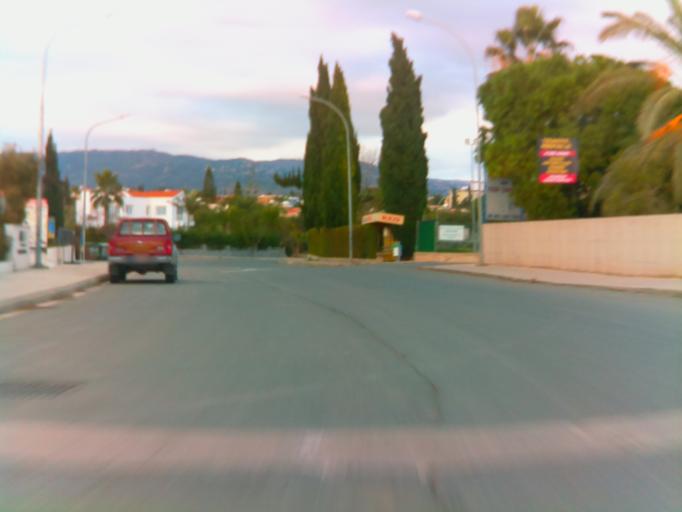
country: CY
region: Pafos
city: Pegeia
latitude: 34.8598
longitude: 32.3601
